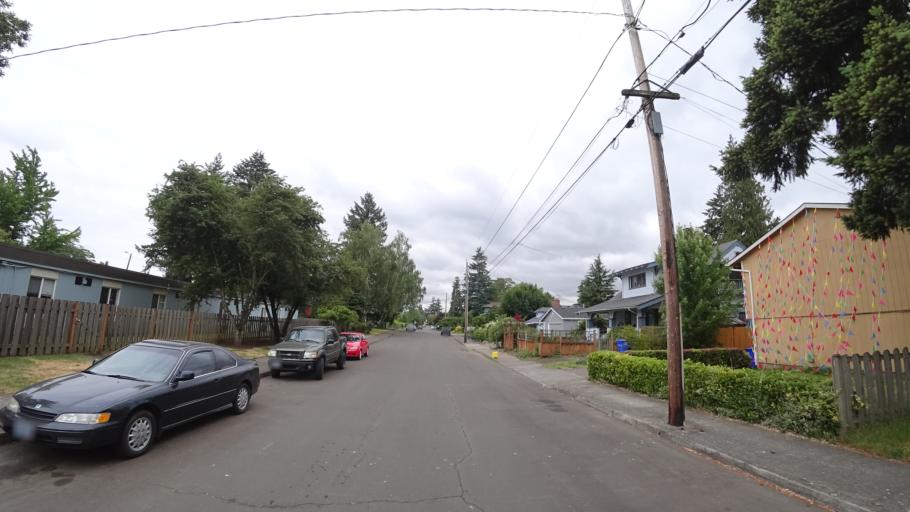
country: US
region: Oregon
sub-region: Multnomah County
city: Lents
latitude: 45.4776
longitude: -122.5852
